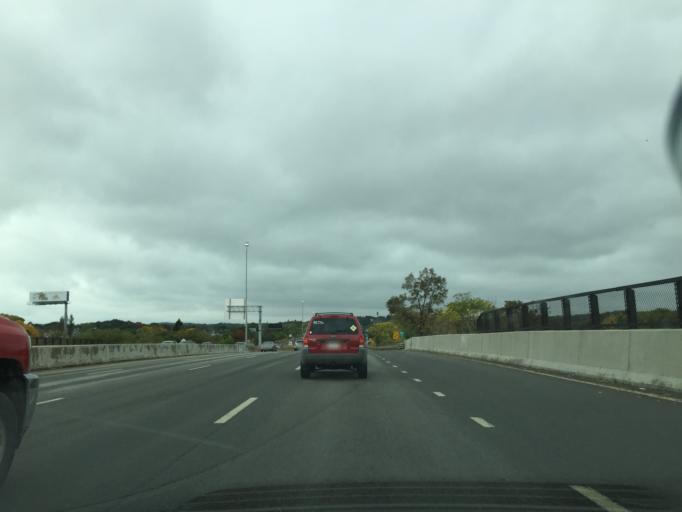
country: US
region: Massachusetts
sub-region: Middlesex County
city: Medford
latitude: 42.4059
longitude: -71.0991
